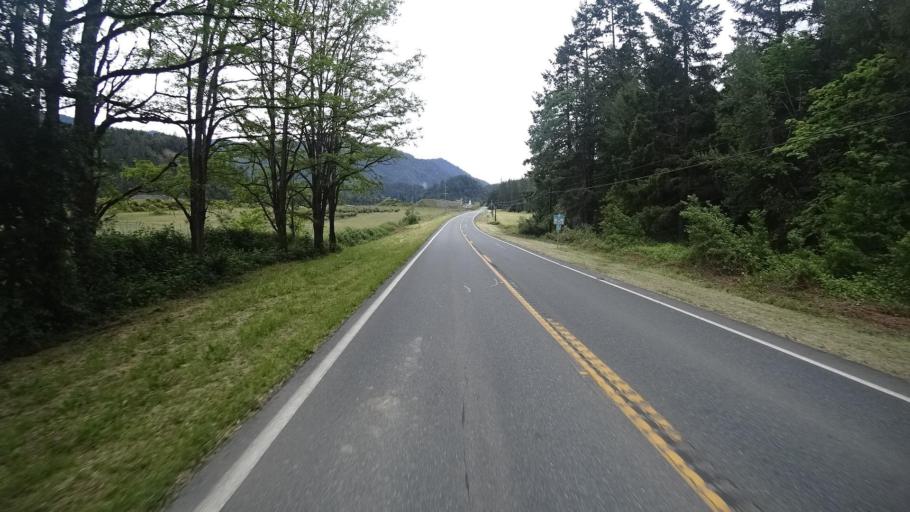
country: US
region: California
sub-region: Humboldt County
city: Willow Creek
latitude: 40.9529
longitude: -123.6411
